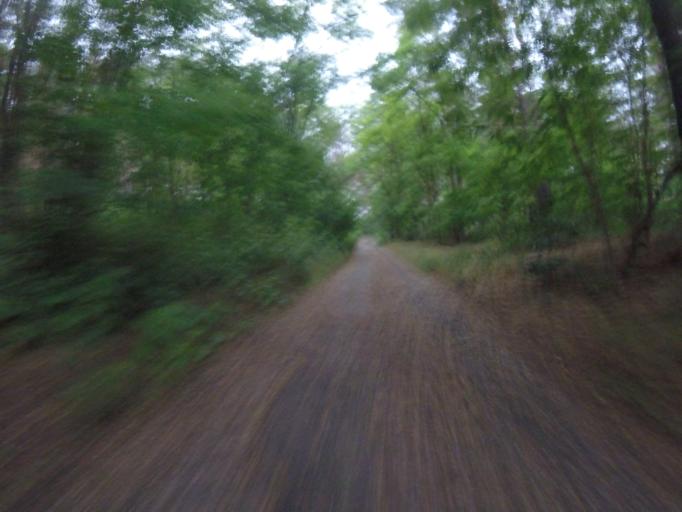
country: DE
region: Brandenburg
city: Bestensee
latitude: 52.2231
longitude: 13.7072
